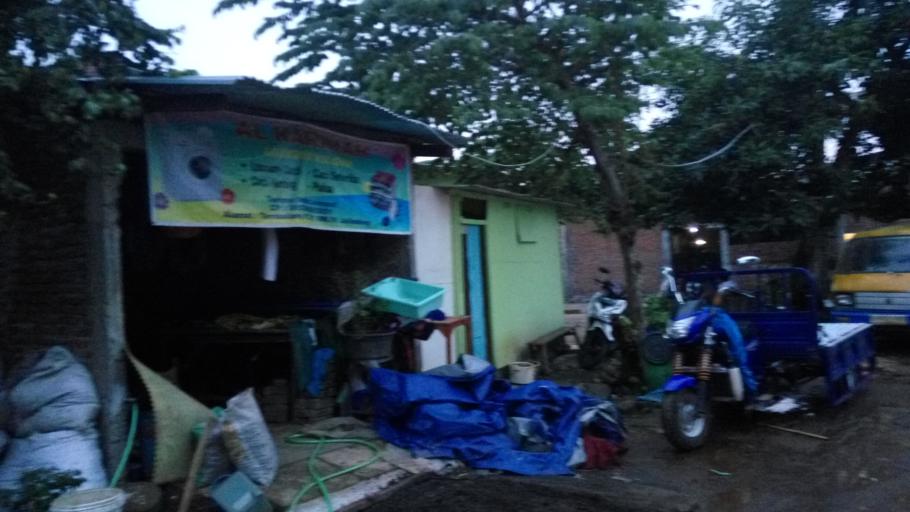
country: ID
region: Central Java
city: Semarang
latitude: -7.0495
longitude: 110.4459
